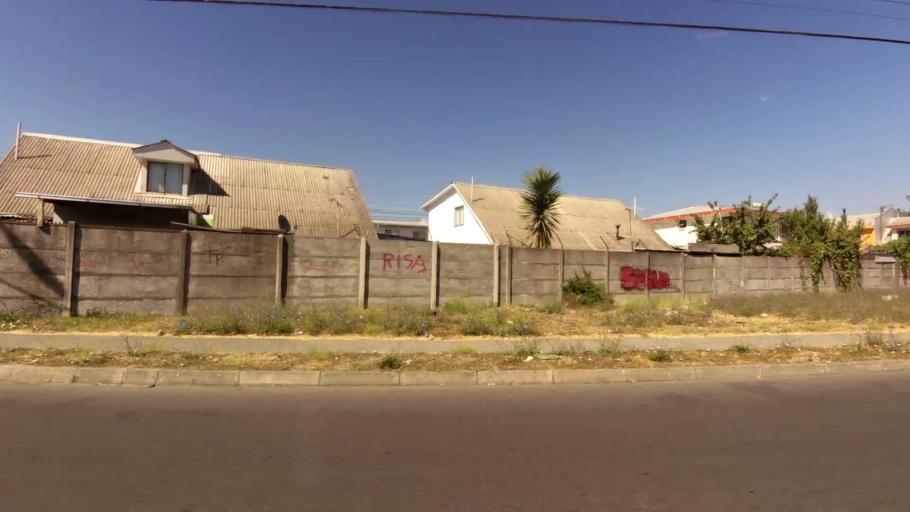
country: CL
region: Maule
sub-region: Provincia de Curico
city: Curico
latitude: -34.9771
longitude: -71.2546
